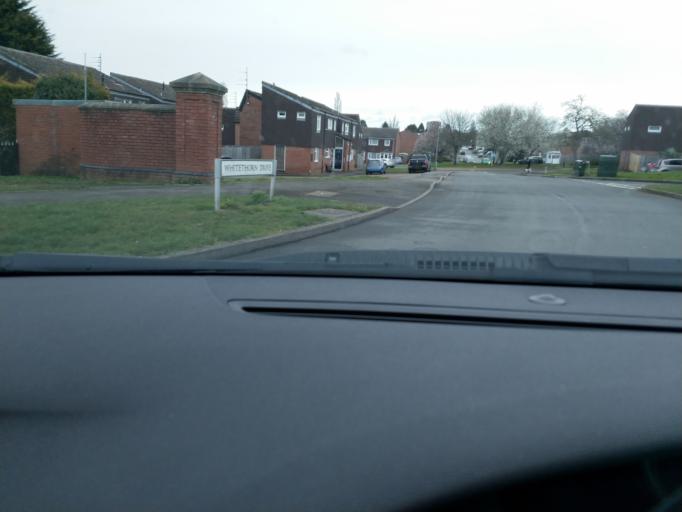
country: GB
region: England
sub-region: Warwickshire
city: Royal Leamington Spa
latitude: 52.2970
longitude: -1.5232
